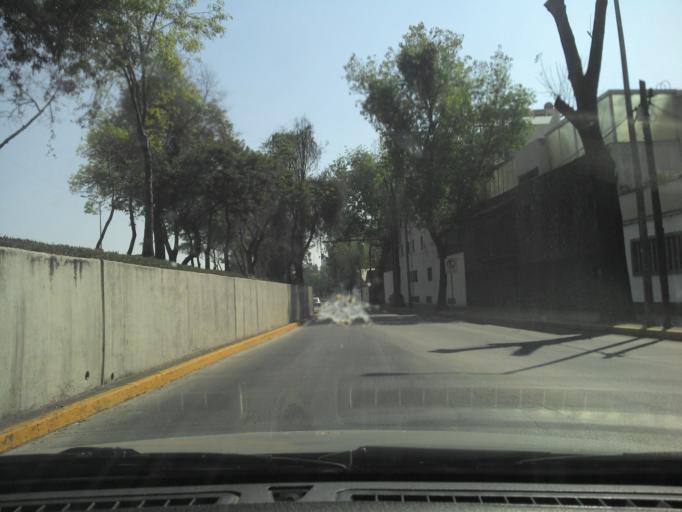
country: MX
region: Mexico City
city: Coyoacan
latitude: 19.3571
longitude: -99.1469
